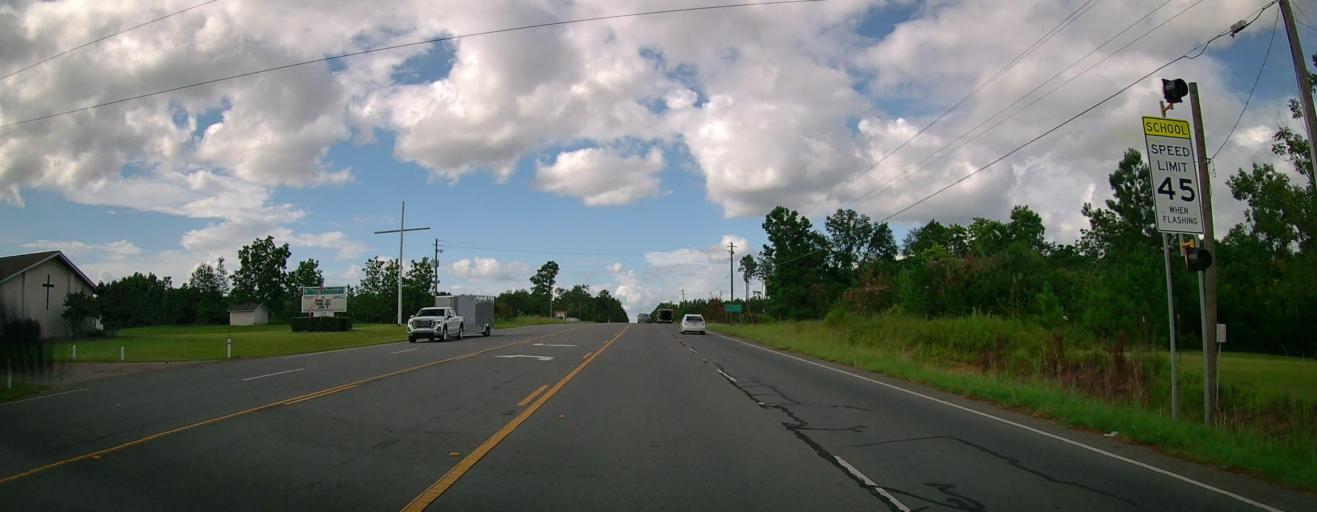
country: US
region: Georgia
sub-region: Coffee County
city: Douglas
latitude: 31.5433
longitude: -82.8510
